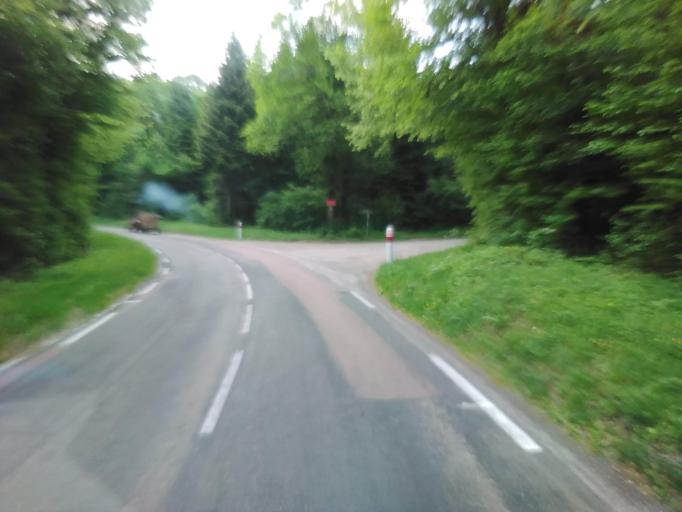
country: FR
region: Franche-Comte
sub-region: Departement du Jura
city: Arbois
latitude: 46.8660
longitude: 5.8051
